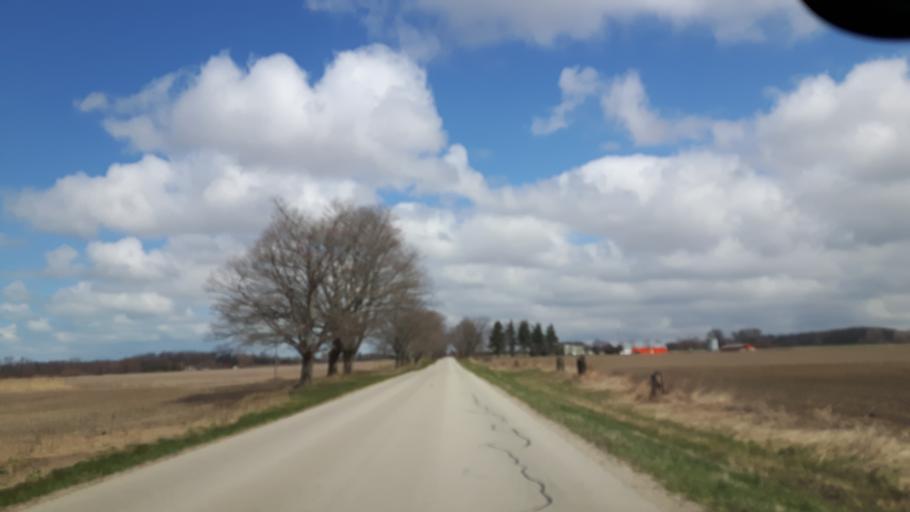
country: CA
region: Ontario
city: Goderich
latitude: 43.6364
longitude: -81.6846
